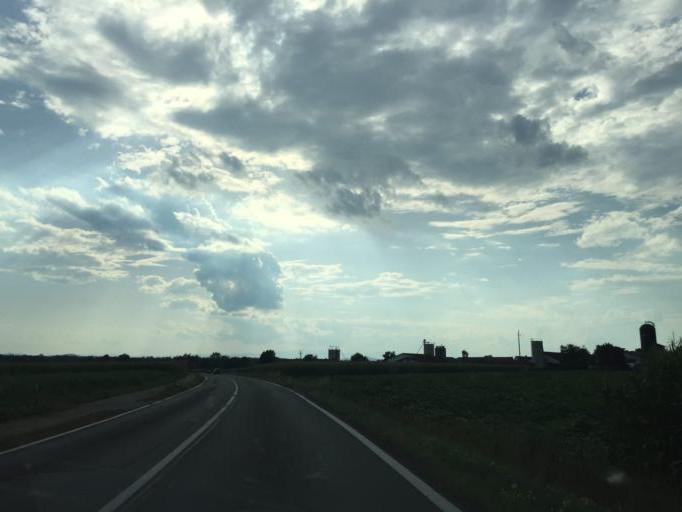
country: AT
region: Styria
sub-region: Politischer Bezirk Suedoststeiermark
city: Weinburg am Sassbach
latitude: 46.7574
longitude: 15.6804
